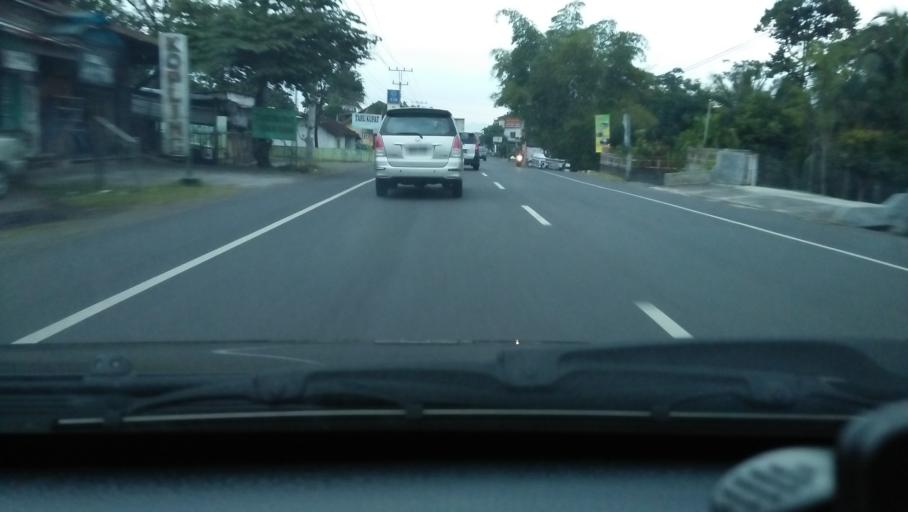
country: ID
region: Central Java
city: Magelang
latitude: -7.4188
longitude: 110.2336
